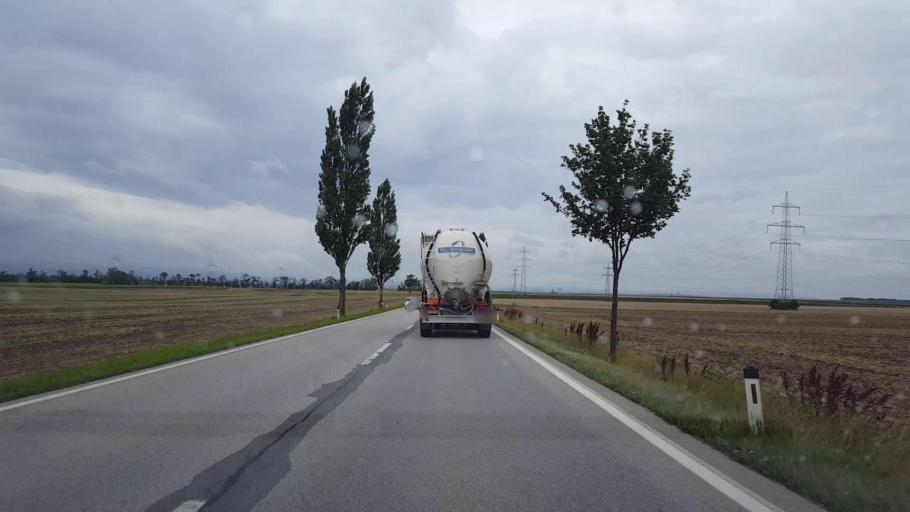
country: AT
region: Lower Austria
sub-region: Politischer Bezirk Wien-Umgebung
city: Ebergassing
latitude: 48.0619
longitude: 16.4929
